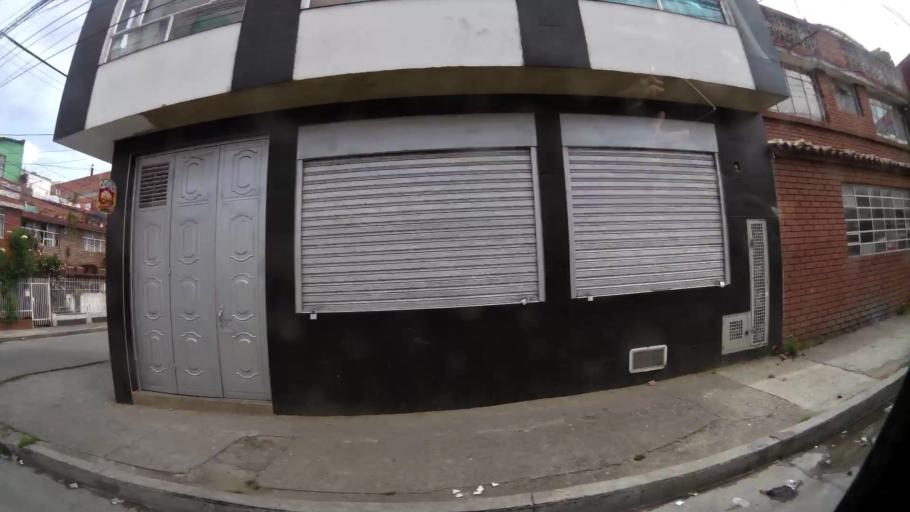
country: CO
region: Bogota D.C.
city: Bogota
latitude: 4.6928
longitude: -74.1125
